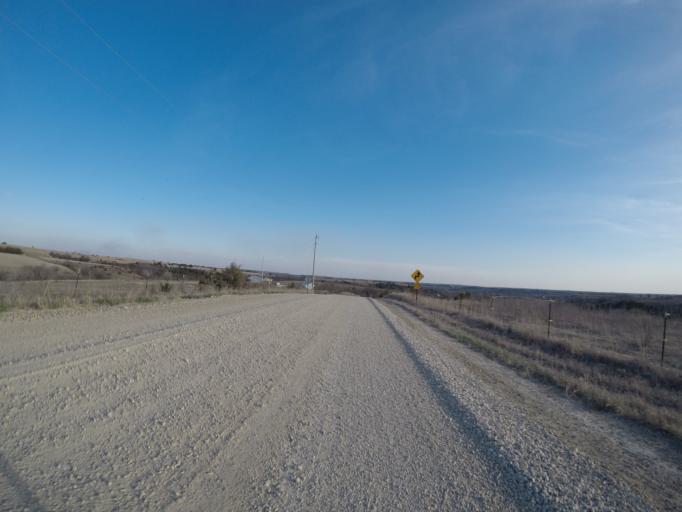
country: US
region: Kansas
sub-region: Riley County
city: Ogden
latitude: 39.2345
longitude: -96.6969
